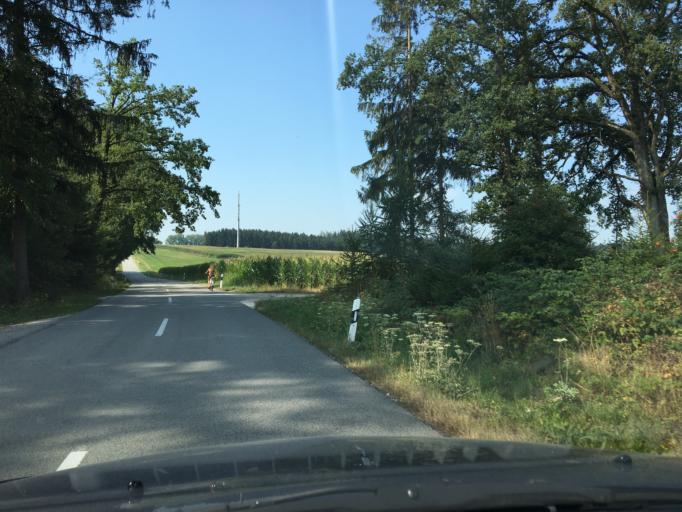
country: DE
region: Bavaria
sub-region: Upper Bavaria
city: Lohkirchen
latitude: 48.3203
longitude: 12.4732
